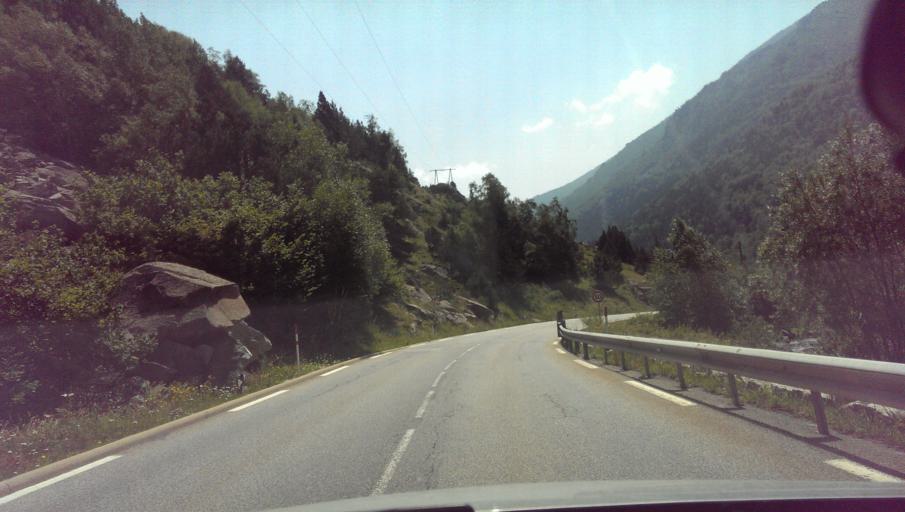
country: ES
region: Catalonia
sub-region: Provincia de Girona
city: Meranges
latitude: 42.5161
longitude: 1.8242
